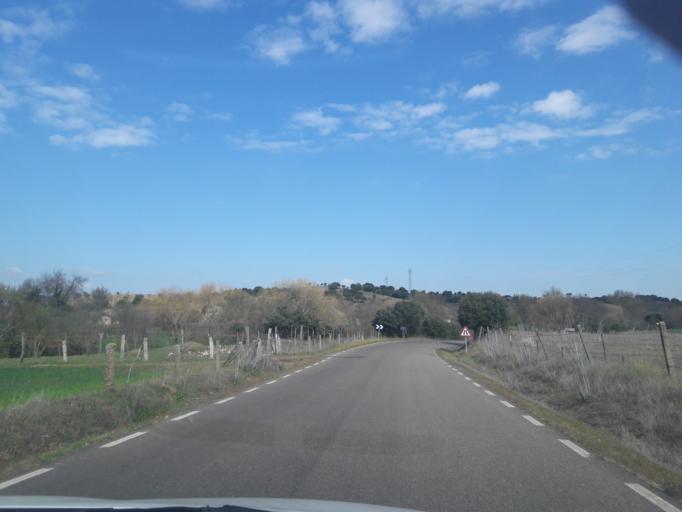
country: ES
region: Castille and Leon
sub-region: Provincia de Salamanca
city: Zamarra
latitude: 40.5661
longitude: -6.4741
